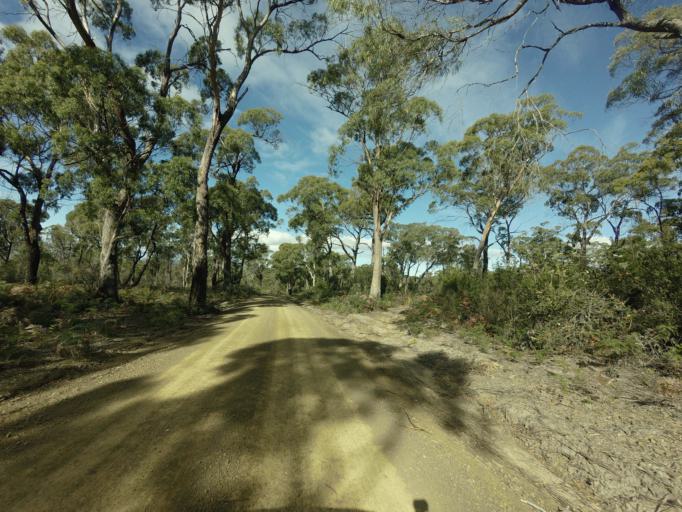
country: AU
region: Tasmania
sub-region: Clarence
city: Sandford
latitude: -42.9727
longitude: 147.7164
